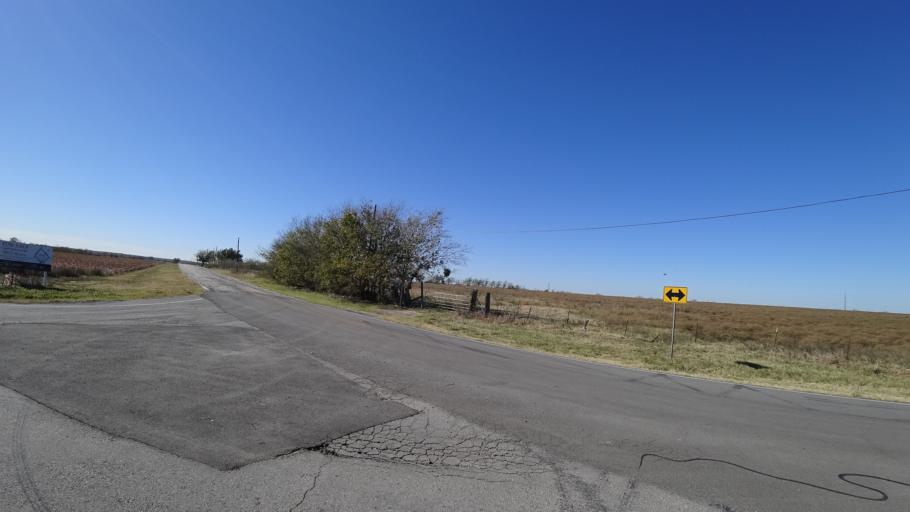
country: US
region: Texas
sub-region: Travis County
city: Garfield
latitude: 30.1107
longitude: -97.6504
